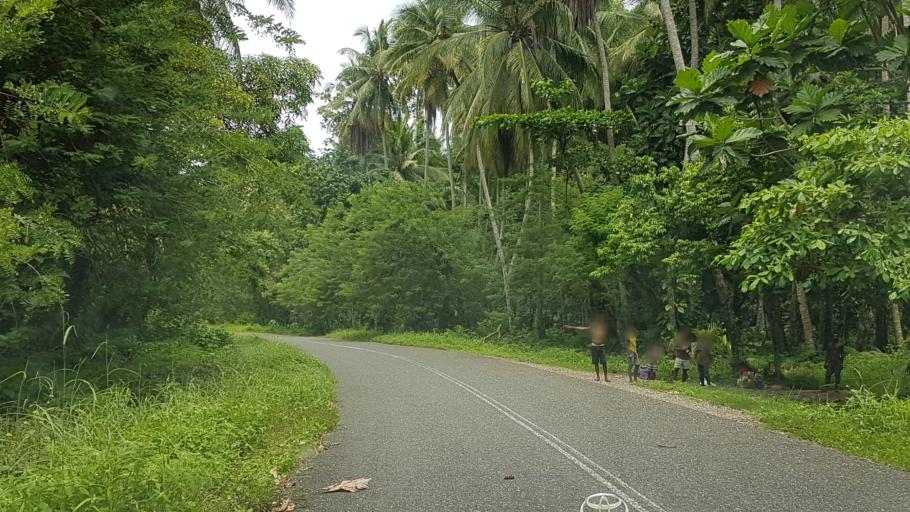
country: PG
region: Madang
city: Madang
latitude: -4.4850
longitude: 145.4225
